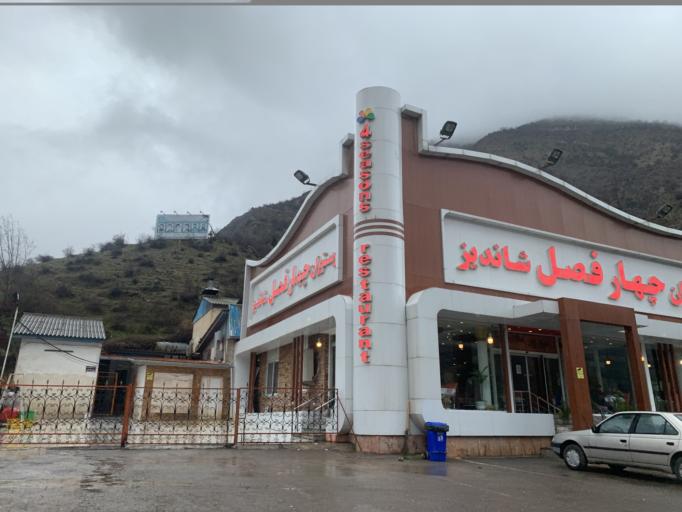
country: IR
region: Mazandaran
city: Amol
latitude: 36.2489
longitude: 52.3688
